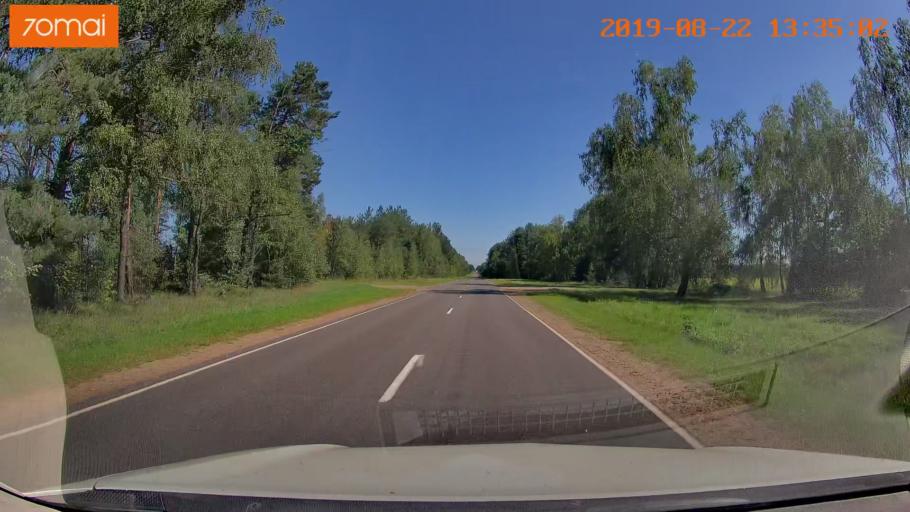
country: BY
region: Minsk
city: Staryya Darohi
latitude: 53.2143
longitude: 28.2571
